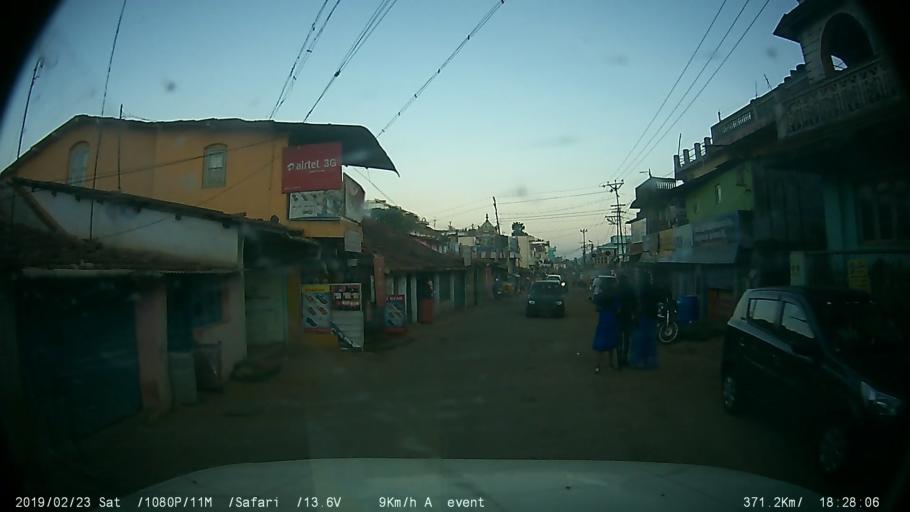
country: IN
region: Tamil Nadu
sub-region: Nilgiri
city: Wellington
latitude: 11.3493
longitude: 76.7810
